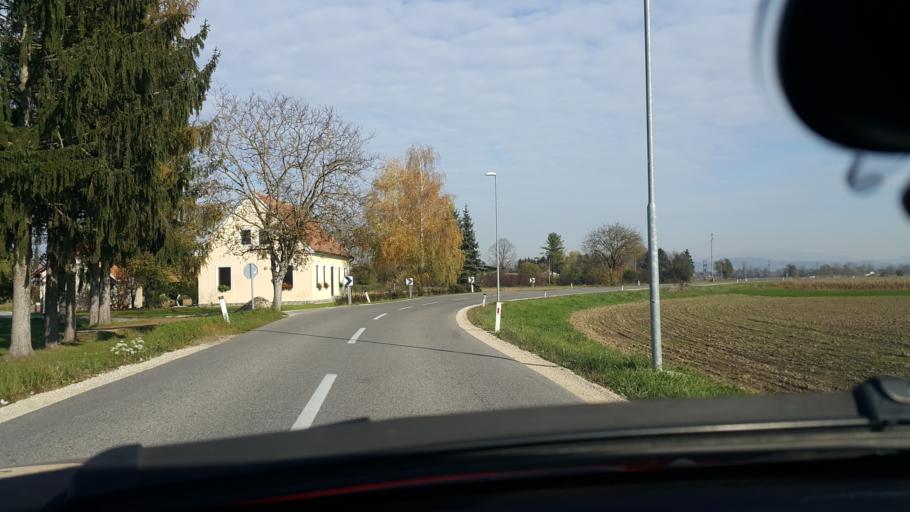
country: SI
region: Brezice
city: Brezice
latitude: 45.9010
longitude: 15.6086
